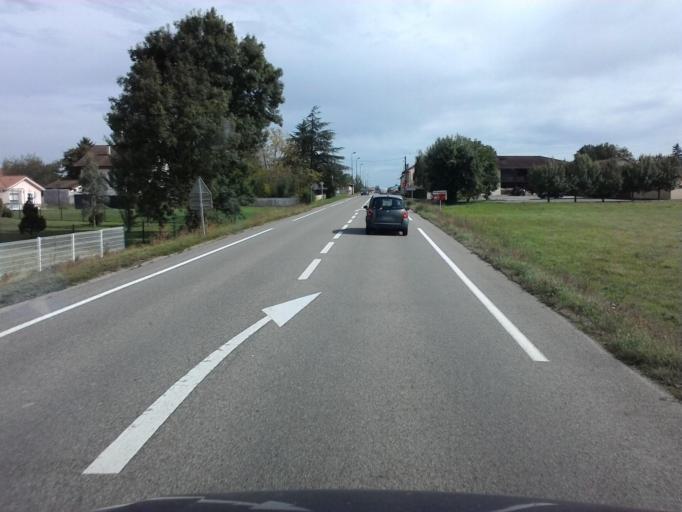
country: FR
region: Rhone-Alpes
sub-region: Departement de l'Ain
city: Polliat
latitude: 46.2500
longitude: 5.1193
